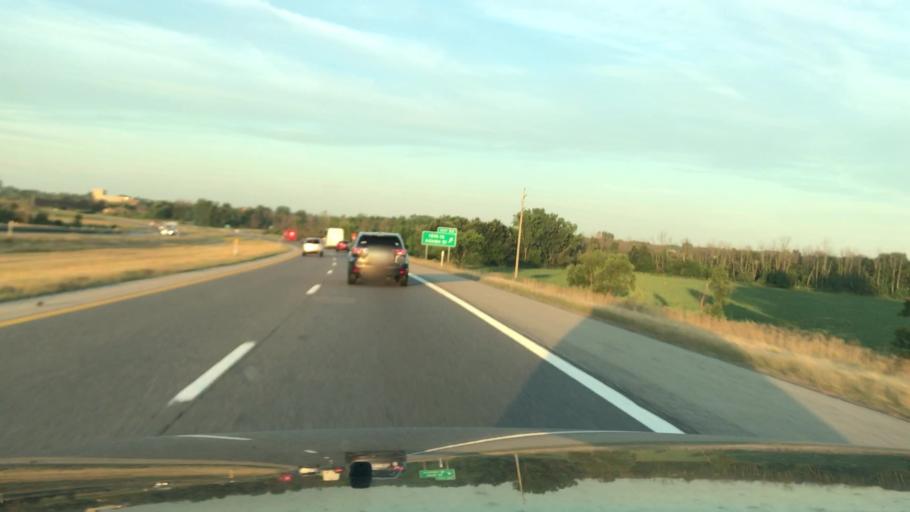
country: US
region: Michigan
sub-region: Ottawa County
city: Zeeland
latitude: 42.7905
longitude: -86.0219
